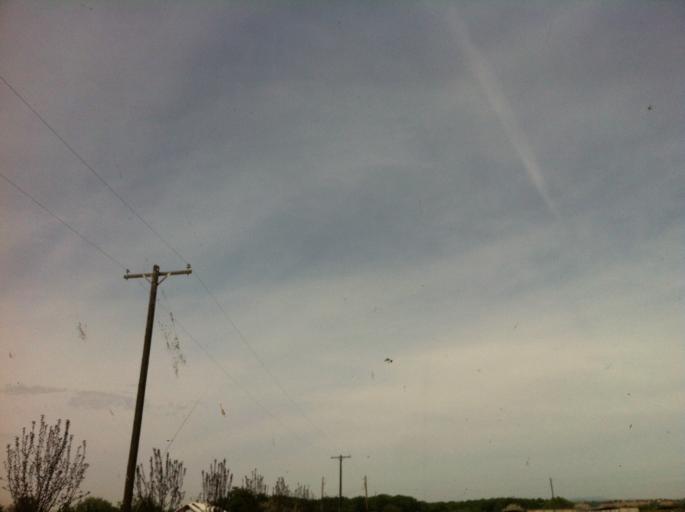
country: US
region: Oregon
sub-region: Malheur County
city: Ontario
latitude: 44.0385
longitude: -116.9335
